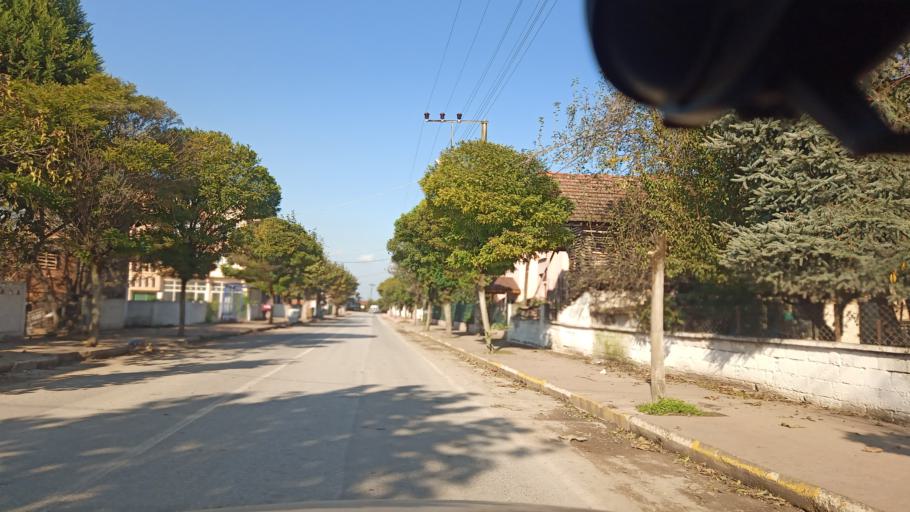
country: TR
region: Sakarya
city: Sogutlu
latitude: 40.9074
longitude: 30.4738
